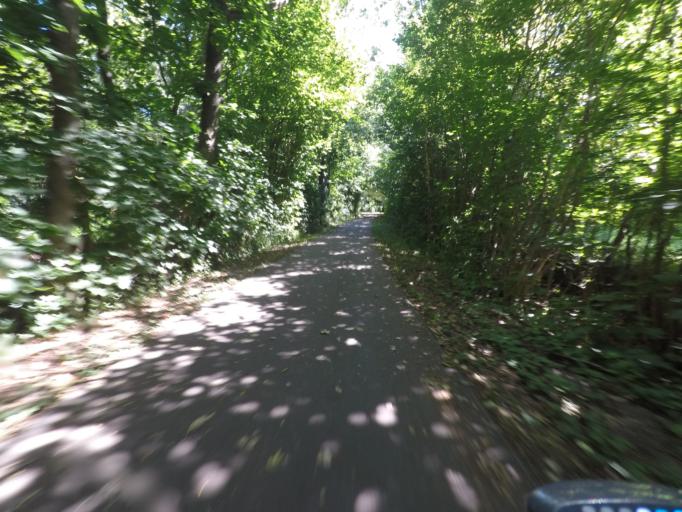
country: DE
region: Schleswig-Holstein
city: Gronwohld
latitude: 53.6351
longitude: 10.3954
